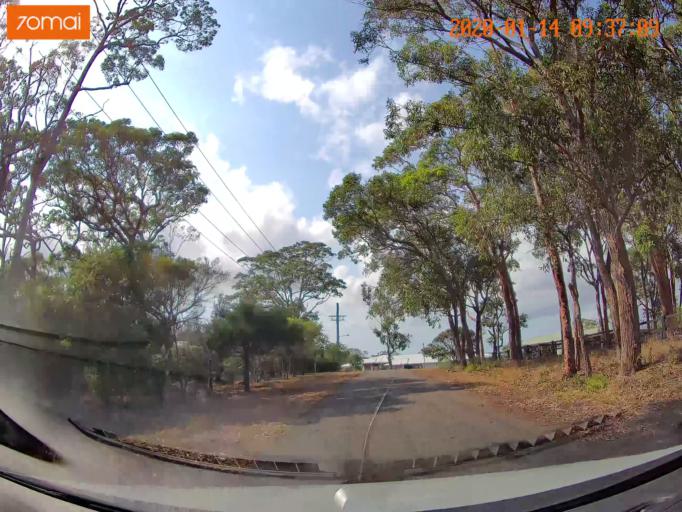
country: AU
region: New South Wales
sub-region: Wyong Shire
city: Kingfisher Shores
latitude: -33.1157
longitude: 151.5593
